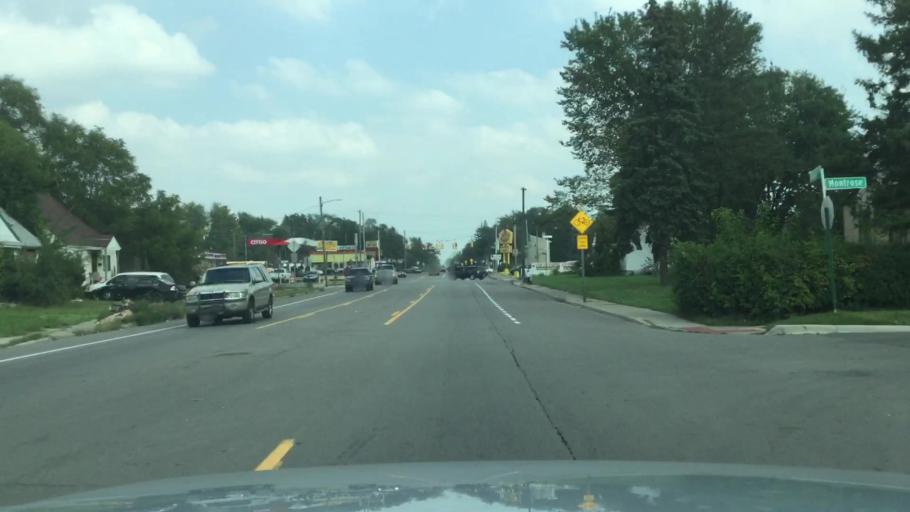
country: US
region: Michigan
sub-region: Wayne County
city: Dearborn
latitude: 42.3653
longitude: -83.1995
